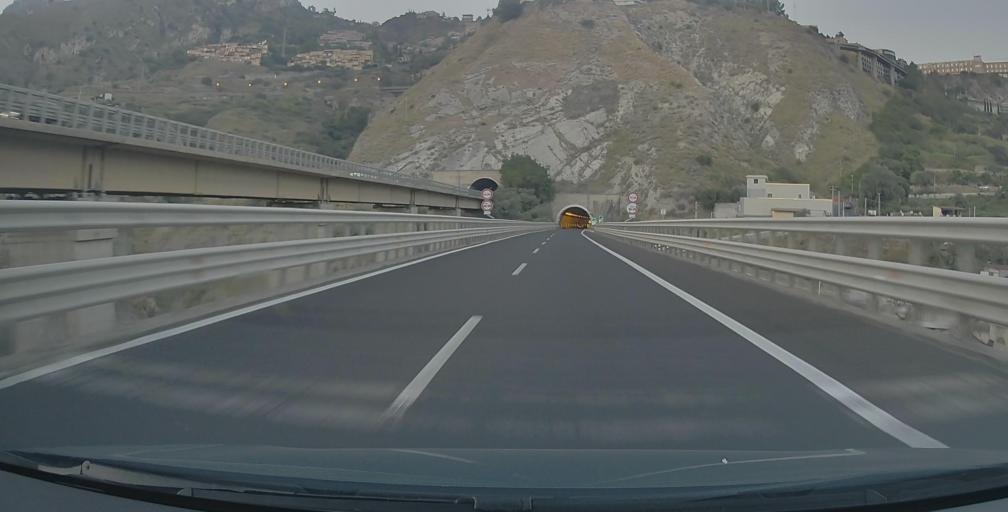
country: IT
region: Sicily
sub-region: Messina
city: Castelmola
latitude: 37.8495
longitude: 15.2753
